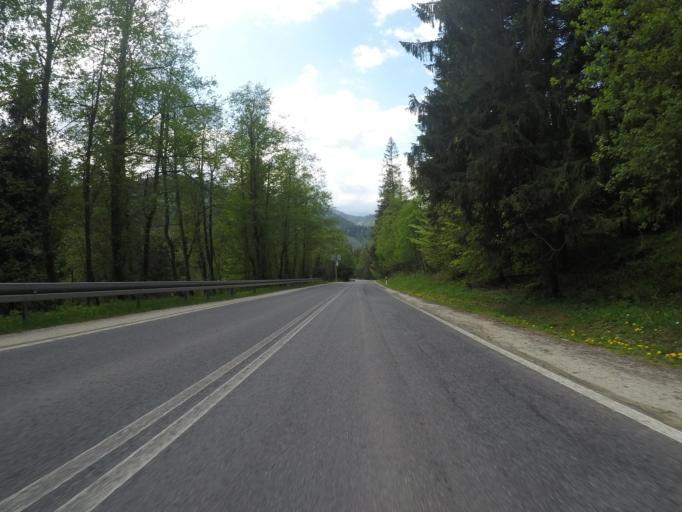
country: PL
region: Lesser Poland Voivodeship
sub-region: Powiat tatrzanski
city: Bukowina Tatrzanska
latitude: 49.2708
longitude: 20.1200
